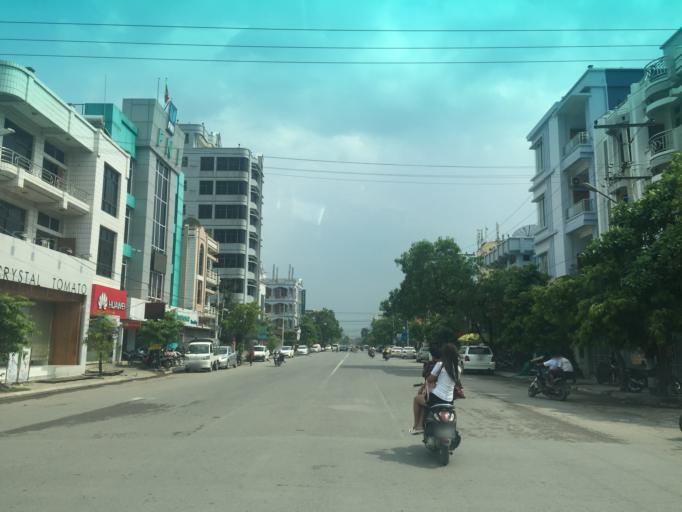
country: MM
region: Mandalay
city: Mandalay
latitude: 21.9734
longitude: 96.0953
